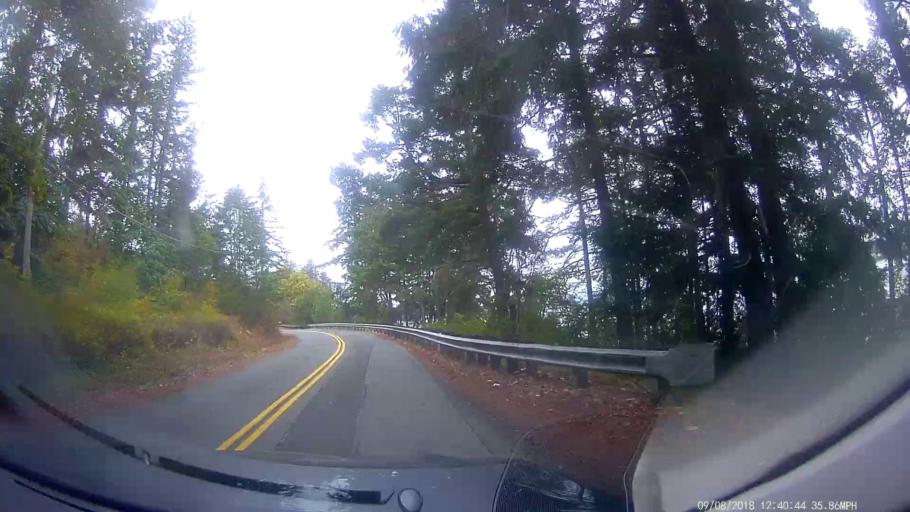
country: US
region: Washington
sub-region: Skagit County
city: Anacortes
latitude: 48.4705
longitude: -122.5863
